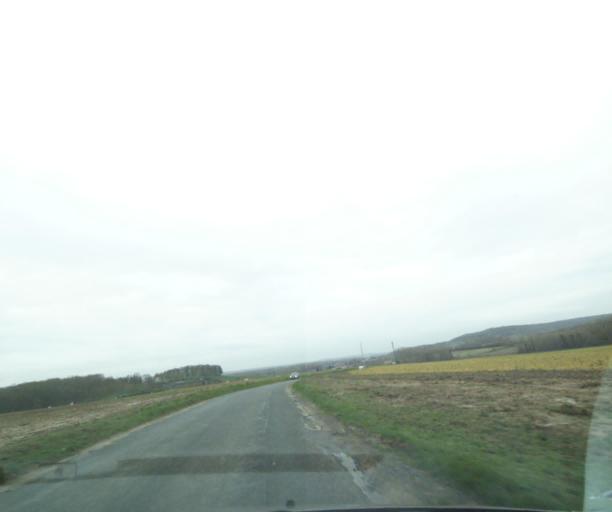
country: FR
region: Picardie
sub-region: Departement de l'Oise
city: Noyon
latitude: 49.5710
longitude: 2.9713
